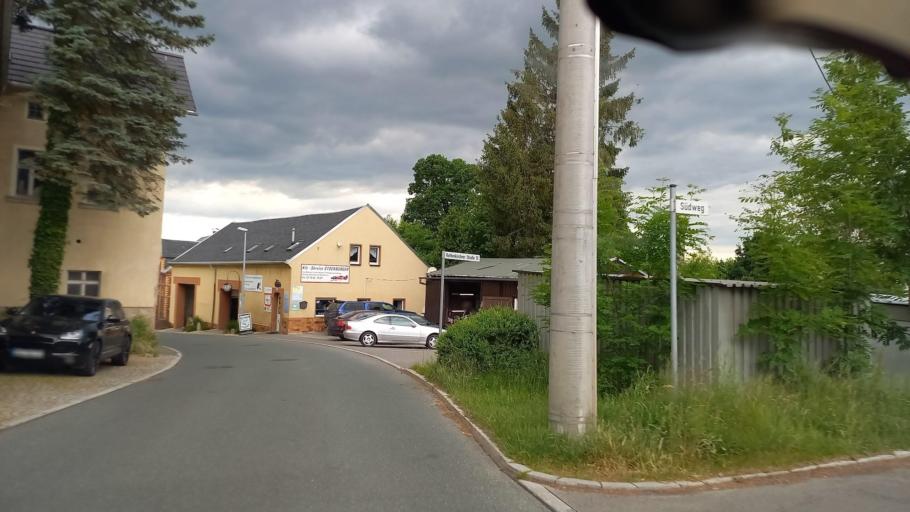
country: DE
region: Saxony
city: Rodewisch
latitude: 50.5539
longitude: 12.4572
